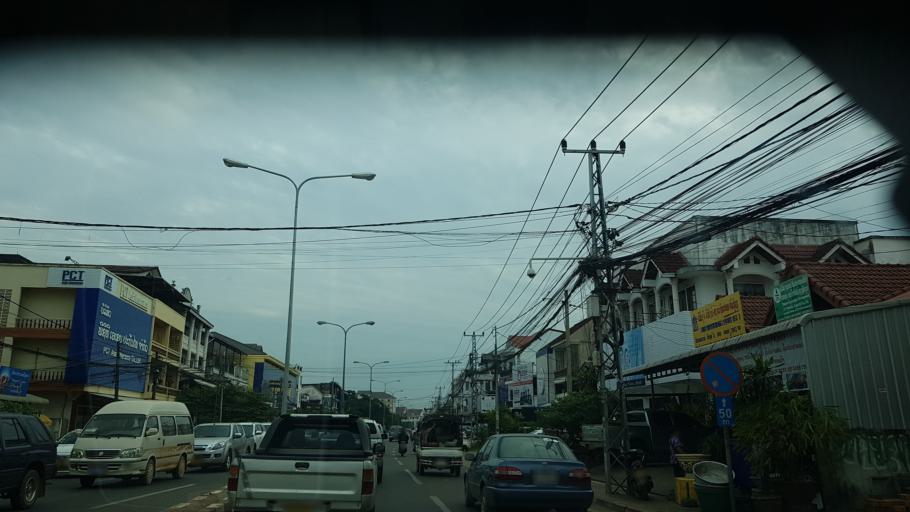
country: LA
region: Vientiane
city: Vientiane
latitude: 17.9532
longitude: 102.6185
